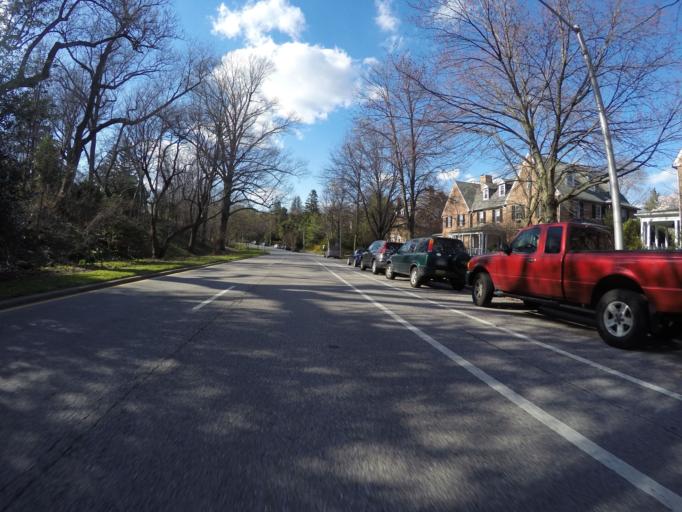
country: US
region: Maryland
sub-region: City of Baltimore
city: Baltimore
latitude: 39.3380
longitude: -76.6261
